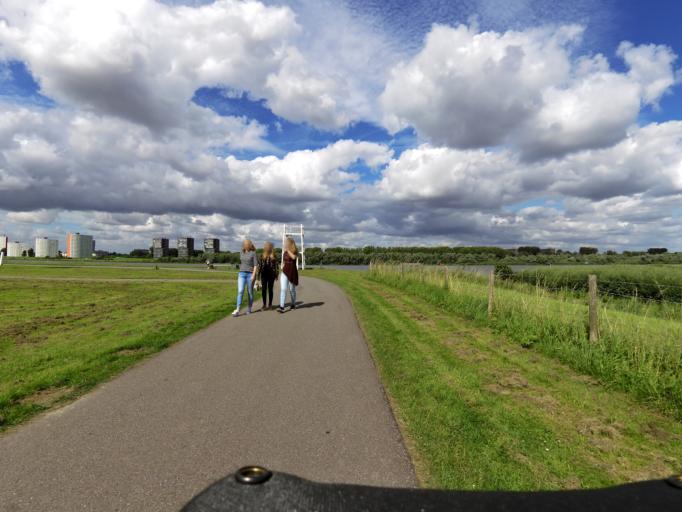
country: NL
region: South Holland
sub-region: Gemeente Spijkenisse
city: Spijkenisse
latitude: 51.8439
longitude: 4.3587
